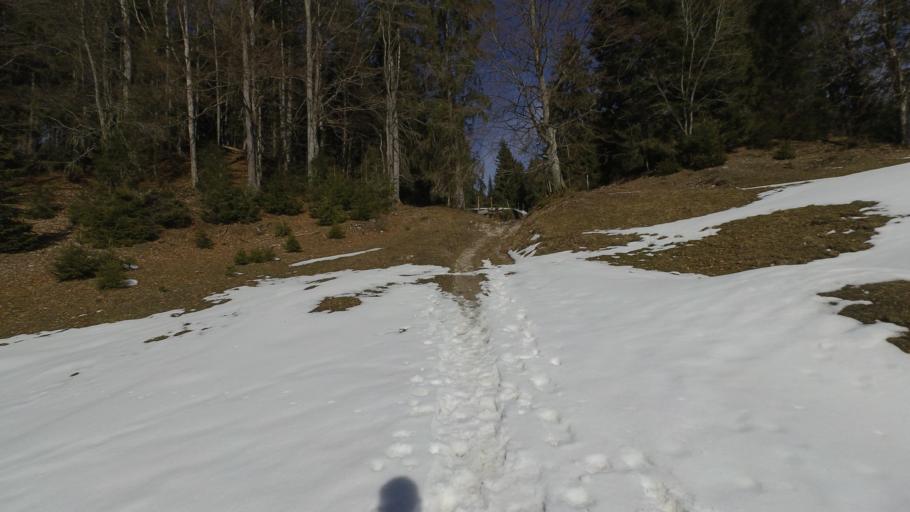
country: DE
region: Bavaria
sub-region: Upper Bavaria
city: Reit im Winkl
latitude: 47.6866
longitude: 12.4446
